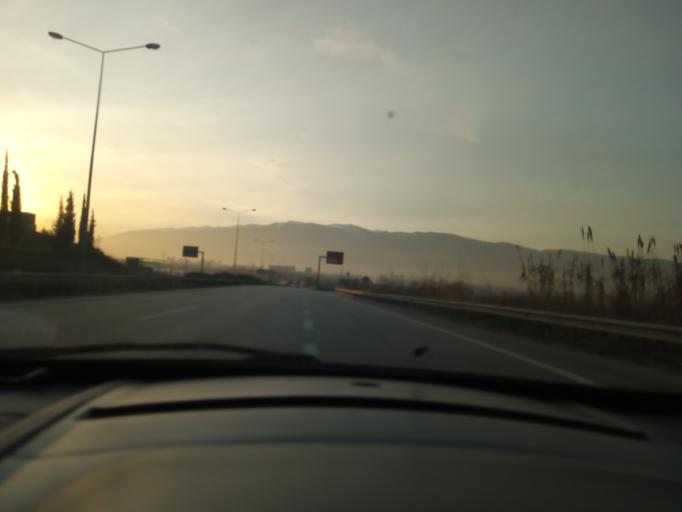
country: TR
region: Bursa
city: Demirtas
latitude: 40.2811
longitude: 29.0414
